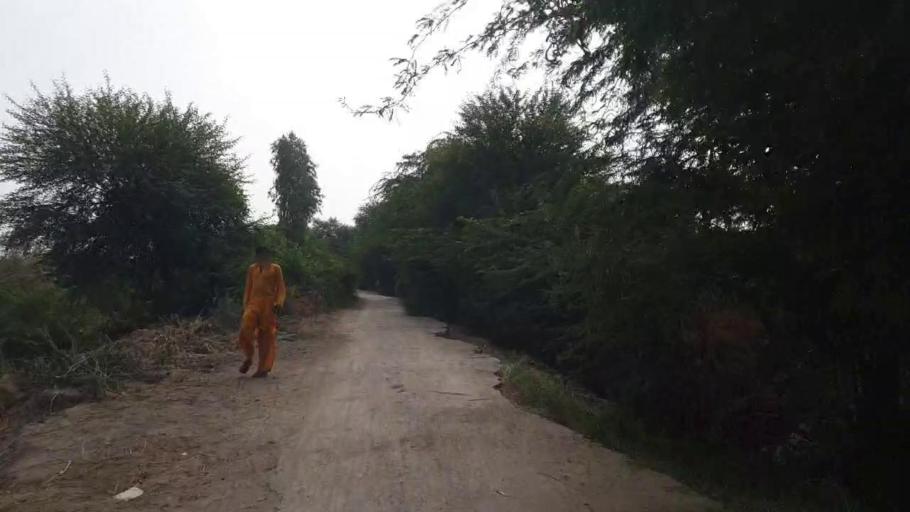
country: PK
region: Sindh
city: Matli
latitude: 24.9992
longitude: 68.7019
